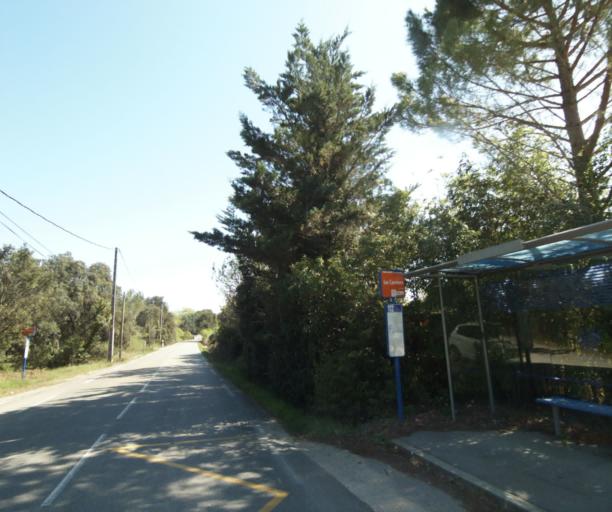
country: FR
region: Languedoc-Roussillon
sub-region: Departement de l'Herault
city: Sussargues
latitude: 43.7014
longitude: 4.0080
